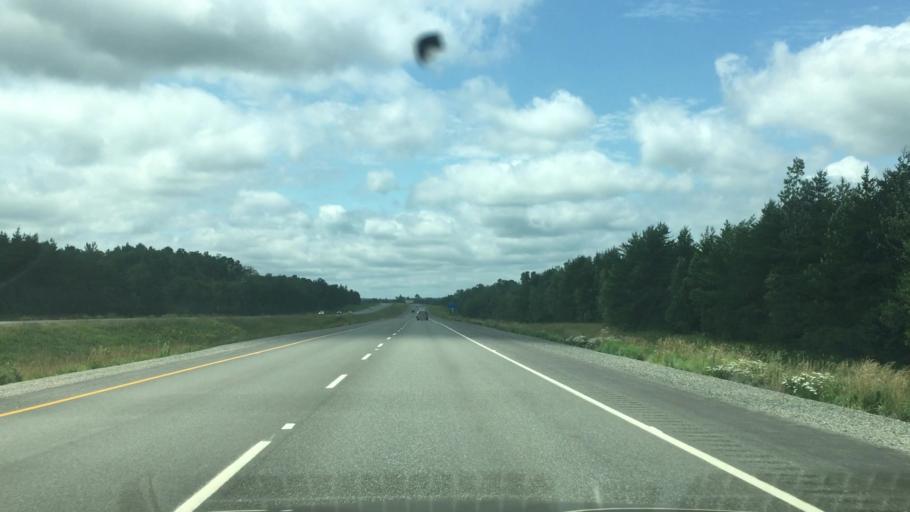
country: CA
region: Nova Scotia
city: Oxford
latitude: 45.7087
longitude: -63.9604
